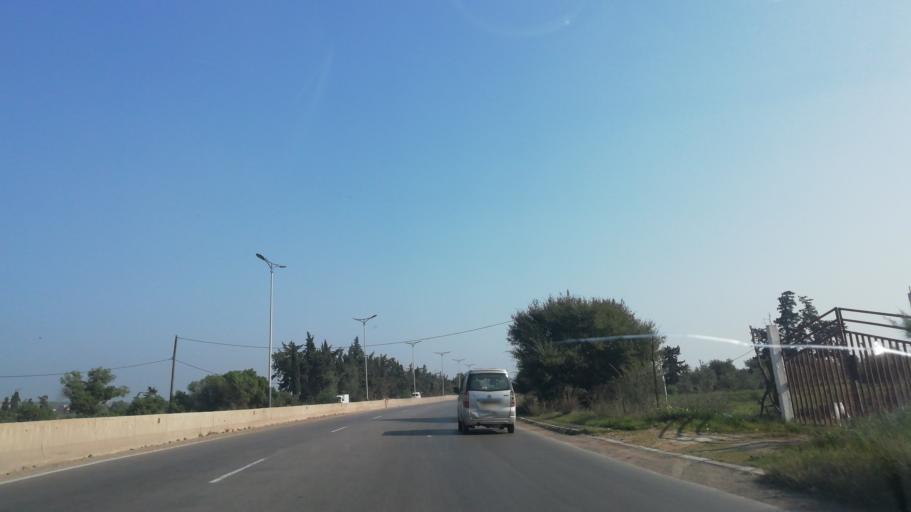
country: DZ
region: Oran
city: Bou Tlelis
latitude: 35.5728
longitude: -0.8785
